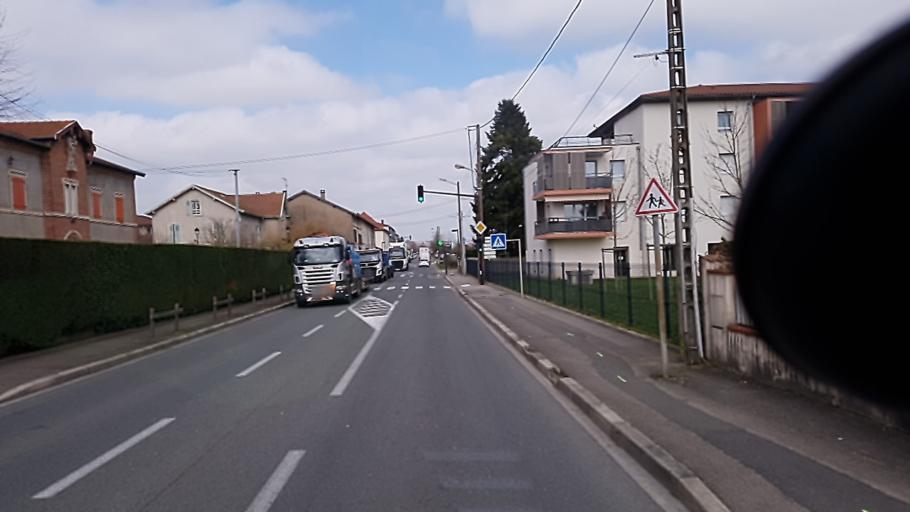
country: FR
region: Rhone-Alpes
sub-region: Departement de l'Ain
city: Villars-les-Dombes
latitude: 46.0009
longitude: 5.0303
